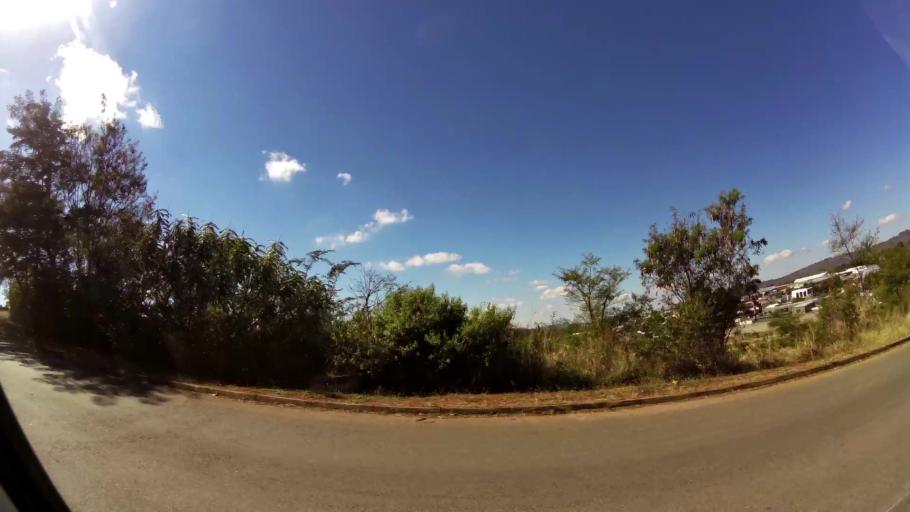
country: ZA
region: Limpopo
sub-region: Mopani District Municipality
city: Tzaneen
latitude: -23.8234
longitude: 30.1538
